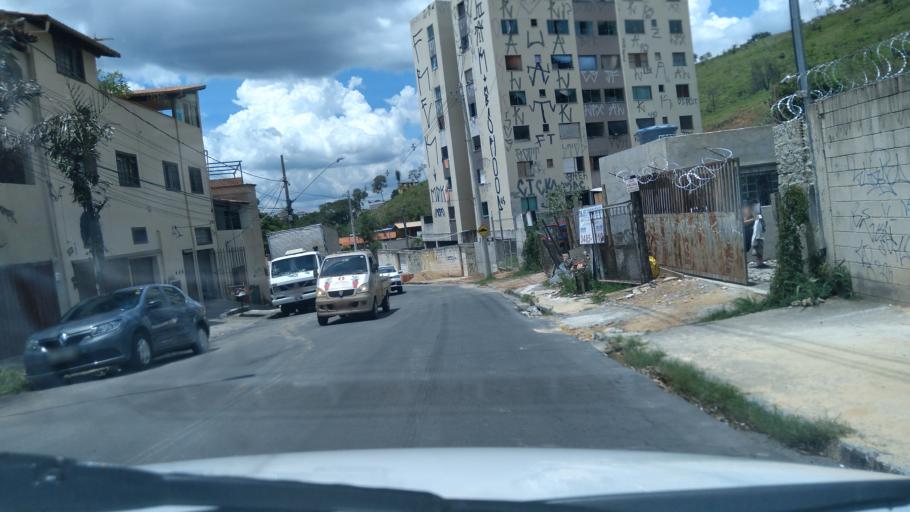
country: BR
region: Minas Gerais
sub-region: Belo Horizonte
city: Belo Horizonte
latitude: -19.8830
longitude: -43.8942
